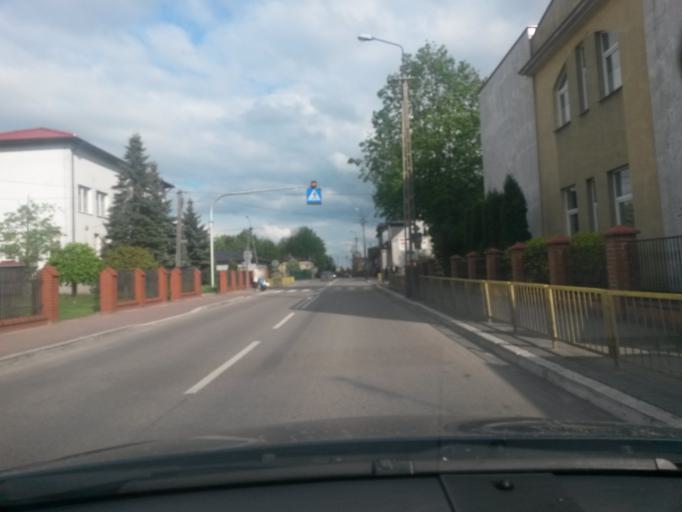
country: PL
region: Masovian Voivodeship
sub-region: Powiat sierpecki
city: Zawidz
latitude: 52.8275
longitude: 19.8704
